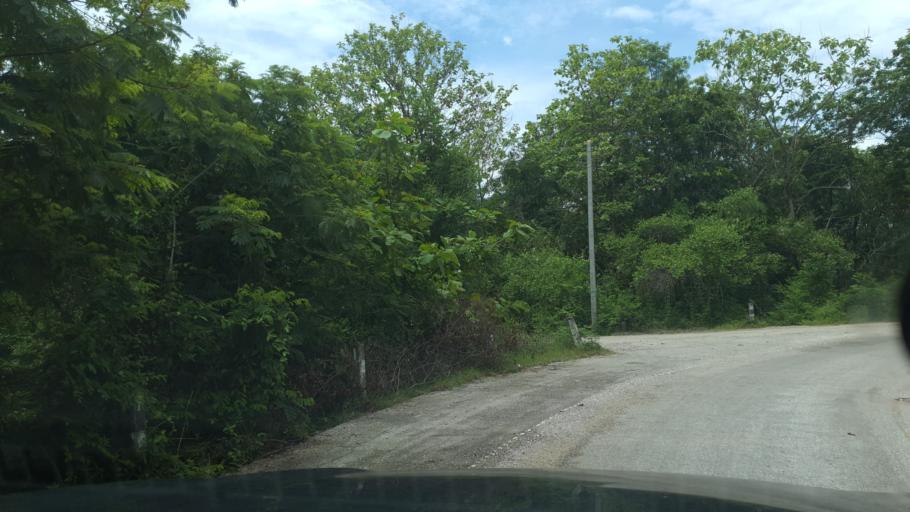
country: TH
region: Lampang
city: Ko Kha
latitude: 18.2527
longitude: 99.3707
